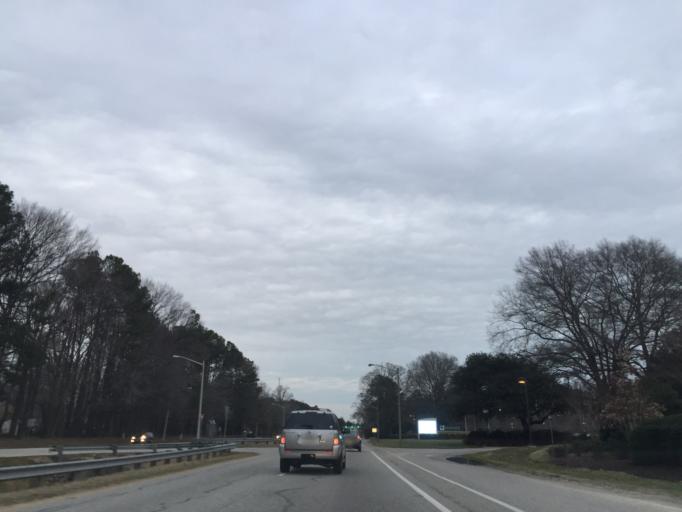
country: US
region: Virginia
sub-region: City of Newport News
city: Newport News
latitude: 37.0644
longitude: -76.4851
